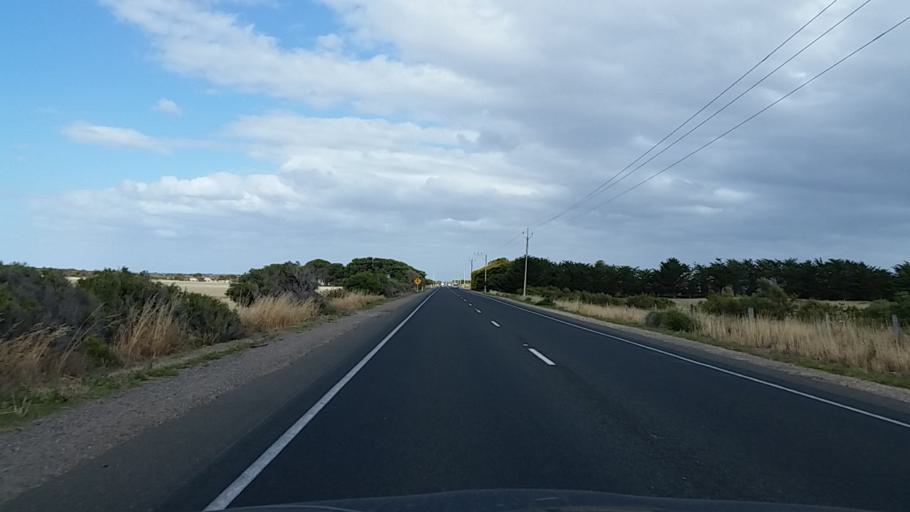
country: AU
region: South Australia
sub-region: Alexandrina
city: Goolwa
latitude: -35.5087
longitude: 138.7317
